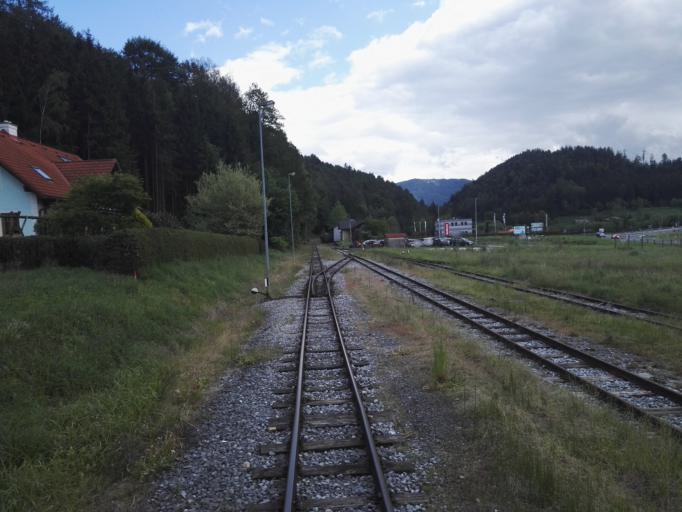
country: AT
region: Styria
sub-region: Politischer Bezirk Weiz
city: Baierdorf-Umgebung
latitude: 47.2617
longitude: 15.7130
